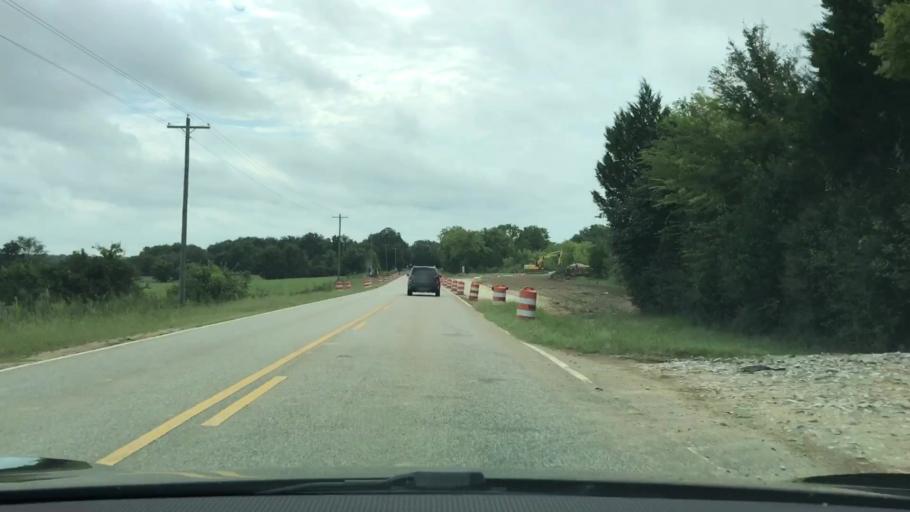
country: US
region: Alabama
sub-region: Montgomery County
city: Pike Road
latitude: 32.2864
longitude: -86.0814
